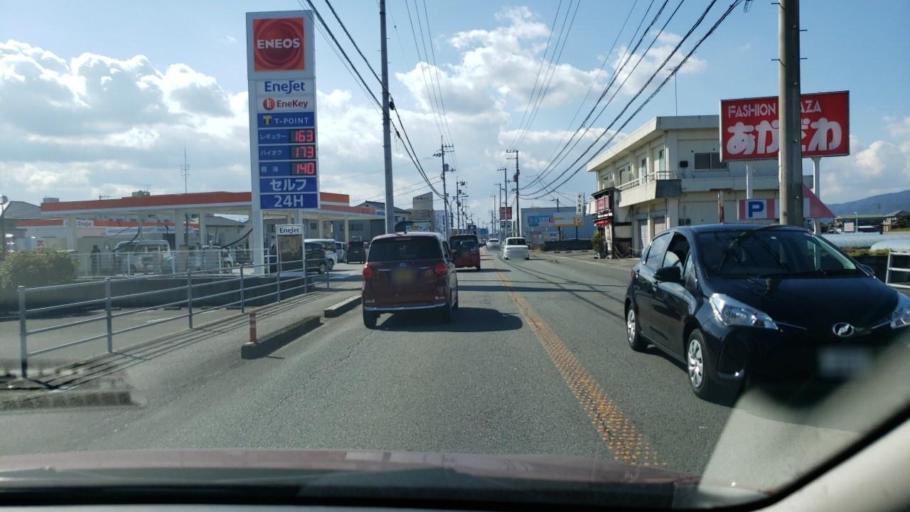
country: JP
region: Tokushima
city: Ishii
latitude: 34.1294
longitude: 134.4822
